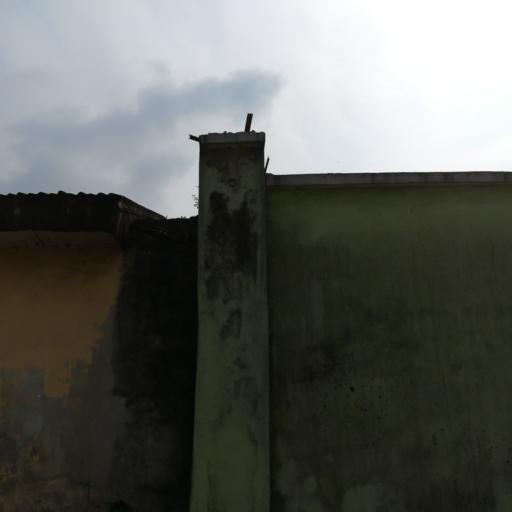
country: NG
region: Rivers
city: Port Harcourt
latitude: 4.8398
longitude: 7.0663
